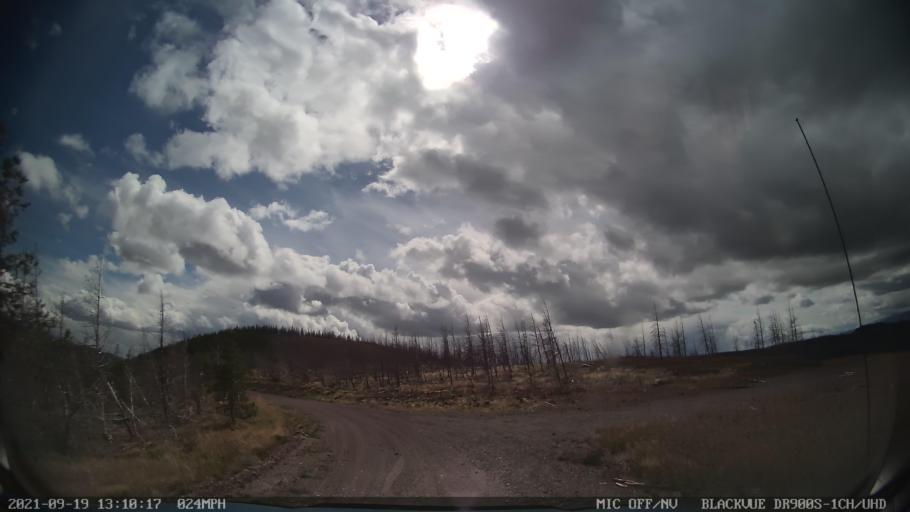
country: US
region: Montana
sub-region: Missoula County
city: Seeley Lake
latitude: 47.1788
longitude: -113.3529
